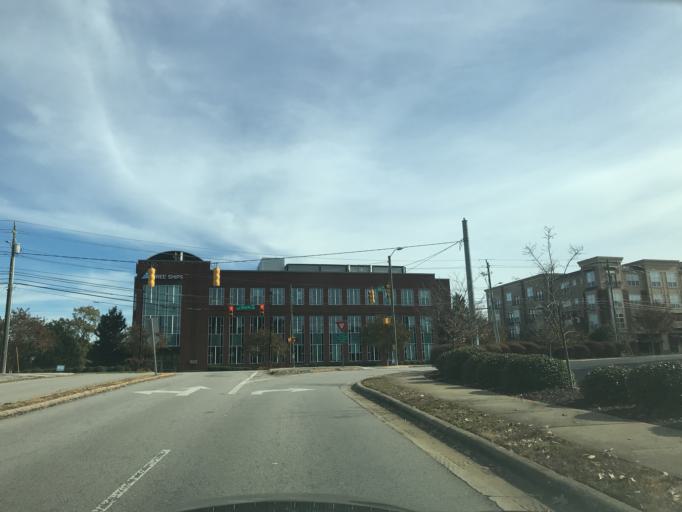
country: US
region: North Carolina
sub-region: Wake County
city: West Raleigh
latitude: 35.7993
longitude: -78.6608
